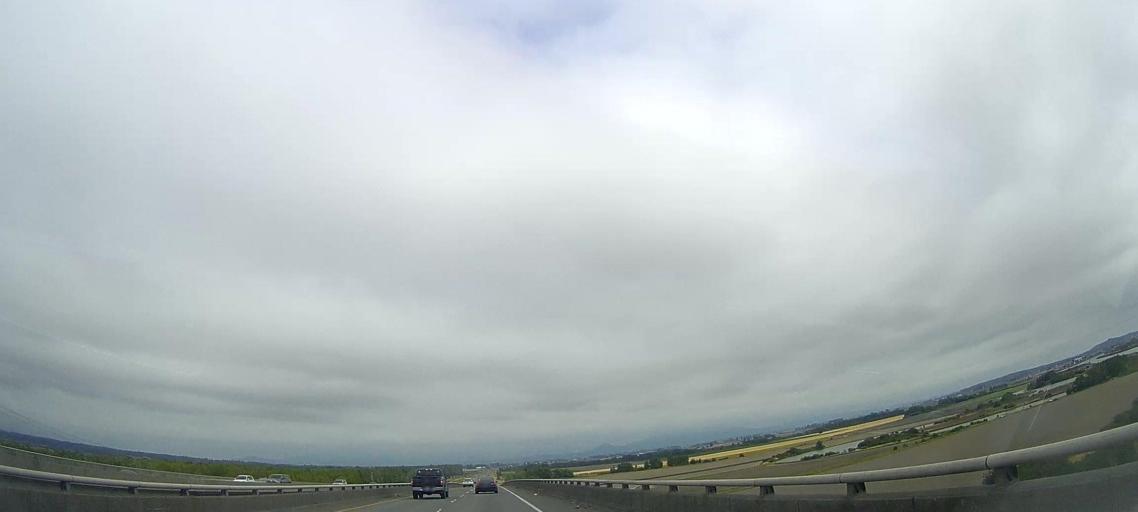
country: US
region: Washington
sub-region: Skagit County
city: Anacortes
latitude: 48.4552
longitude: -122.5138
